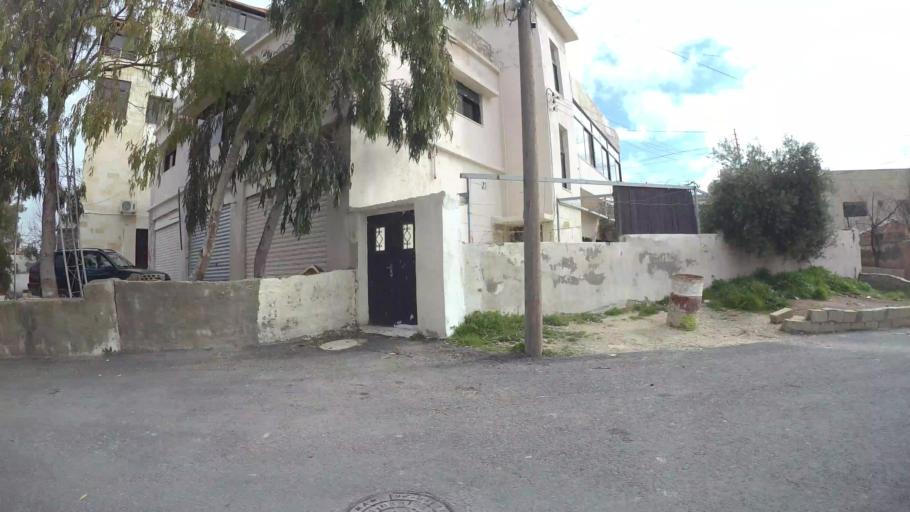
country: JO
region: Amman
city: Al Jubayhah
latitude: 32.0050
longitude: 35.8408
